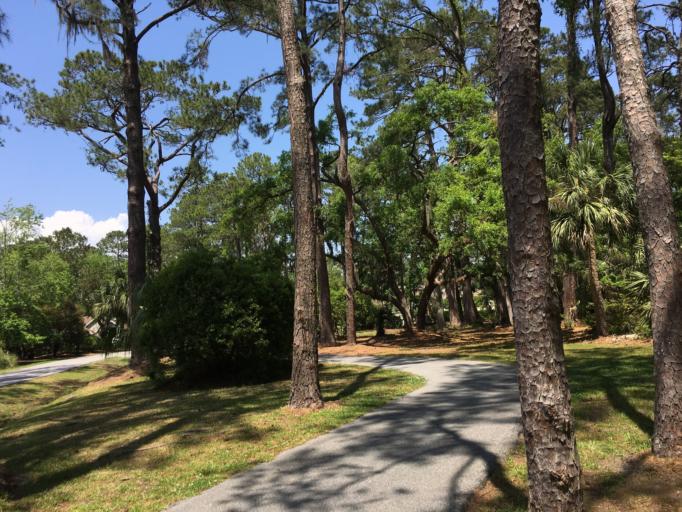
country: US
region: South Carolina
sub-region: Beaufort County
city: Hilton Head Island
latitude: 32.1235
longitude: -80.8110
